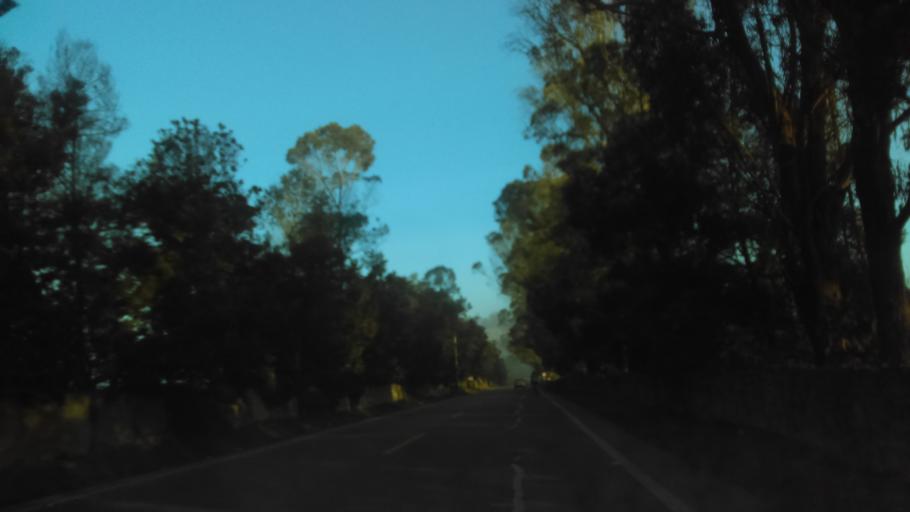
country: CO
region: Cundinamarca
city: Soacha
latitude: 4.6069
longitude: -74.2808
